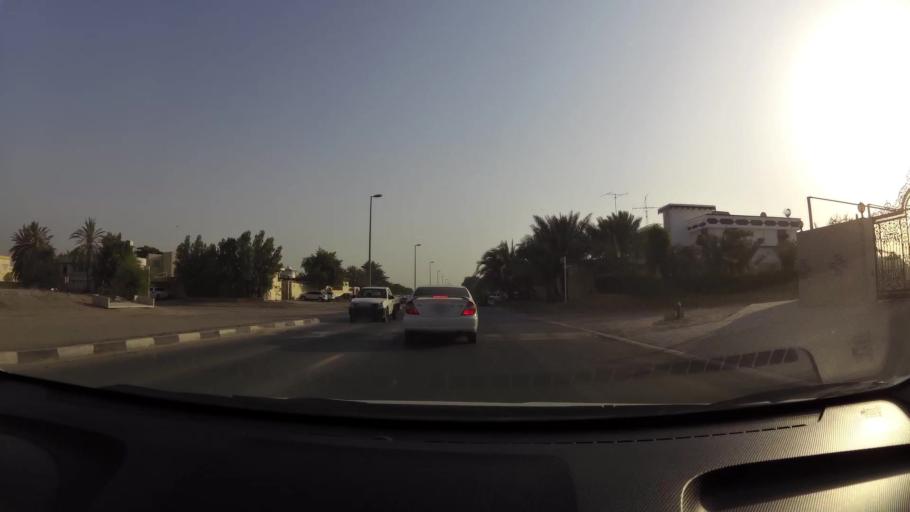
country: AE
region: Ajman
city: Ajman
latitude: 25.3836
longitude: 55.4411
